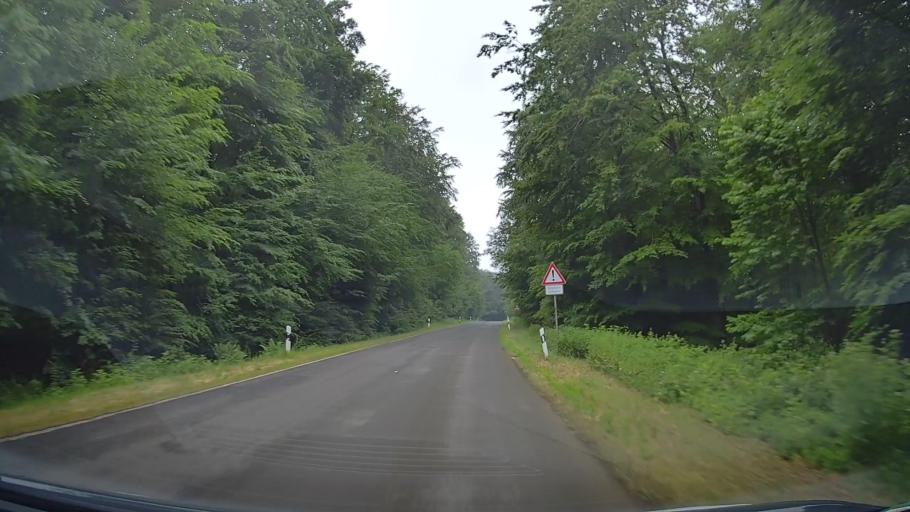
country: DE
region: Lower Saxony
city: Rinteln
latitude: 52.1426
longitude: 9.0426
